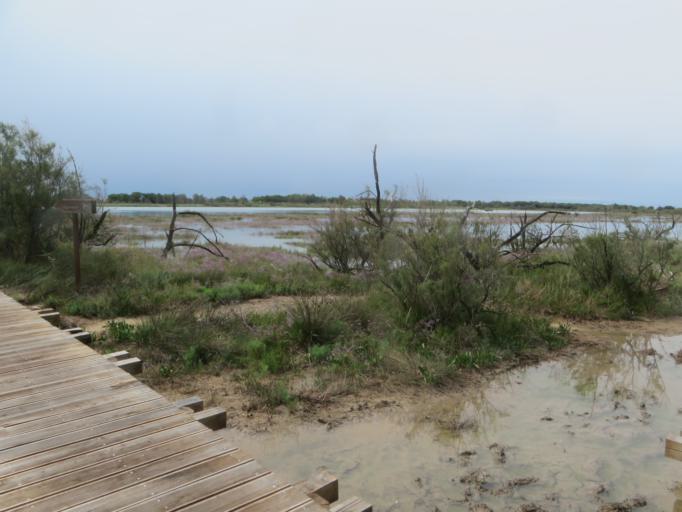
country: IT
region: Veneto
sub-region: Provincia di Venezia
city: Crepaldo
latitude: 45.5391
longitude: 12.7422
